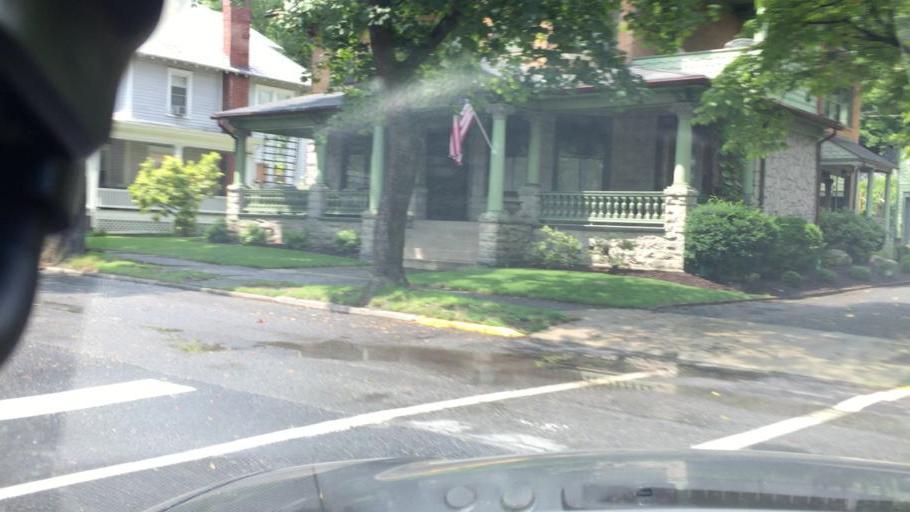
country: US
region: Pennsylvania
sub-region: Monroe County
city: Stroudsburg
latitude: 40.9895
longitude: -75.1949
